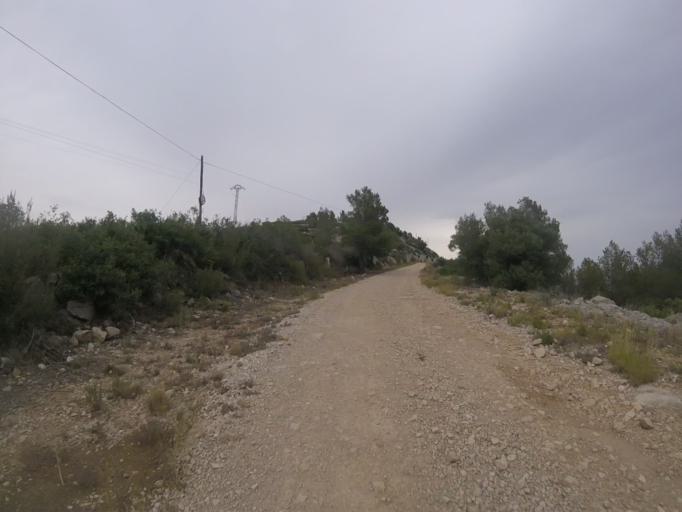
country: ES
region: Valencia
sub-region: Provincia de Castello
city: Alcoceber
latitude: 40.2743
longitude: 0.2788
